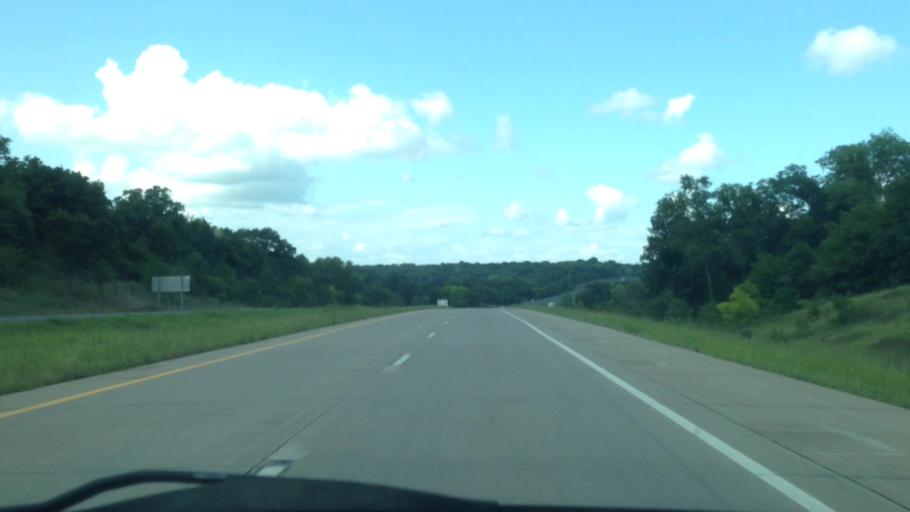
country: US
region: Missouri
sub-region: Lewis County
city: Canton
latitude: 40.1465
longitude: -91.5386
